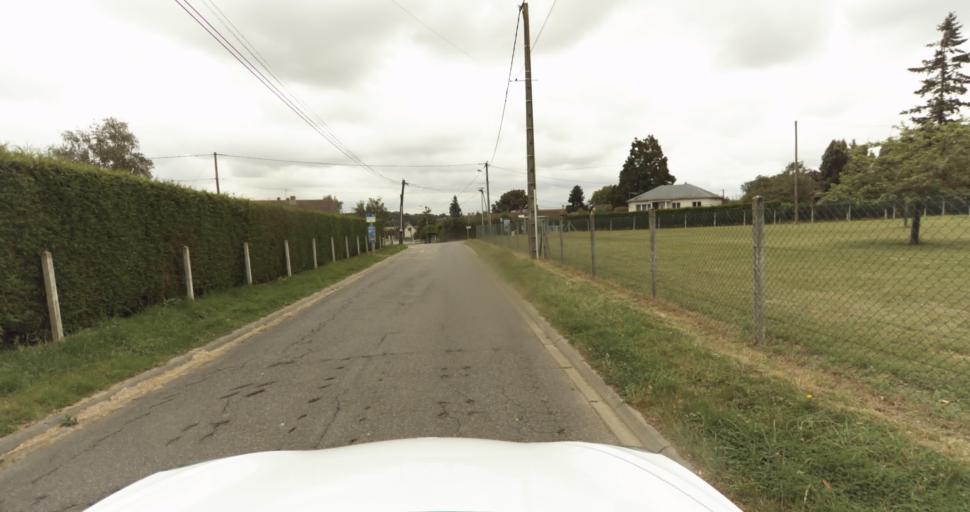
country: FR
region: Haute-Normandie
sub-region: Departement de l'Eure
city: Saint-Sebastien-de-Morsent
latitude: 49.0087
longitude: 1.0644
